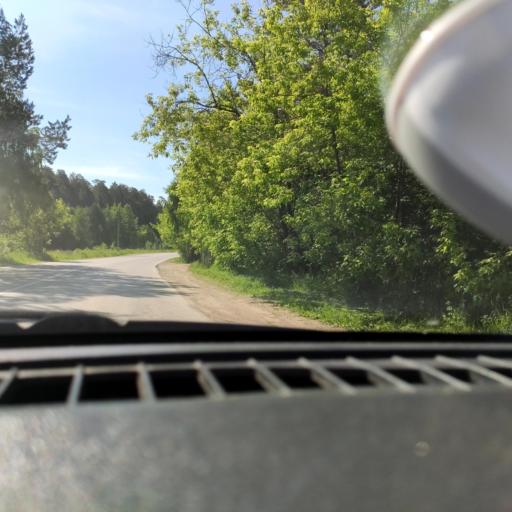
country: RU
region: Perm
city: Overyata
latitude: 58.0087
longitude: 55.8747
